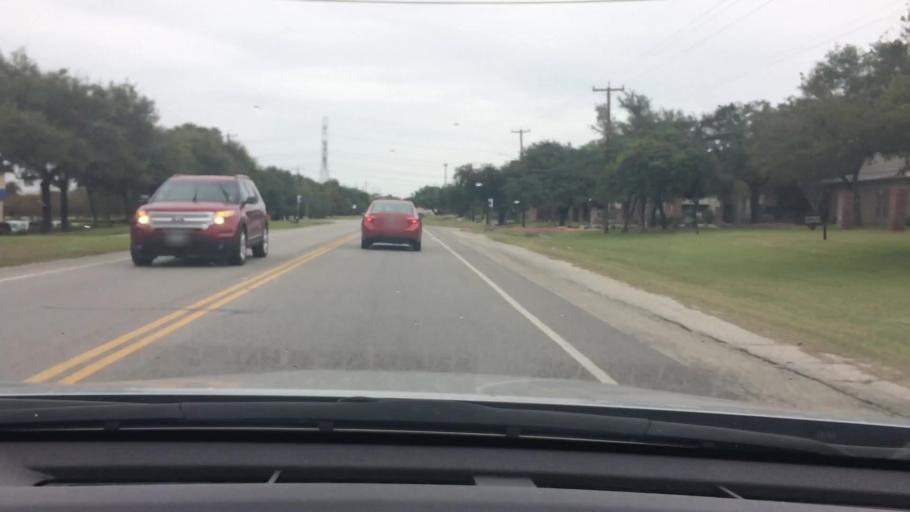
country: US
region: Texas
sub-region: Bexar County
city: Windcrest
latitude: 29.5400
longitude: -98.3705
